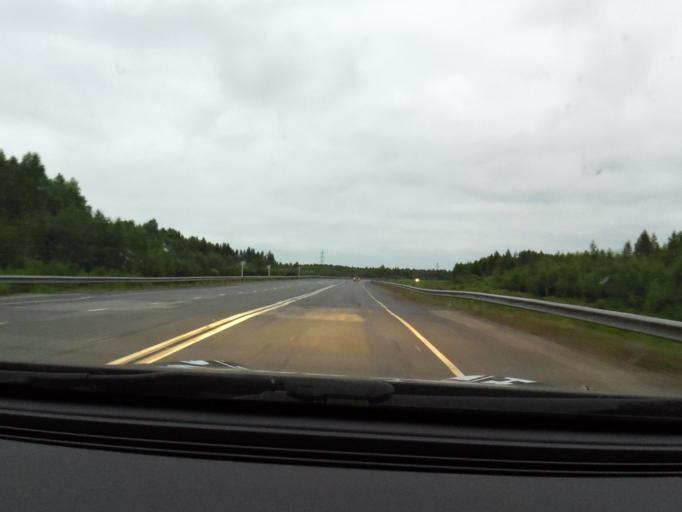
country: RU
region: Perm
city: Krasnokamsk
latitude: 58.0964
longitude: 55.7360
